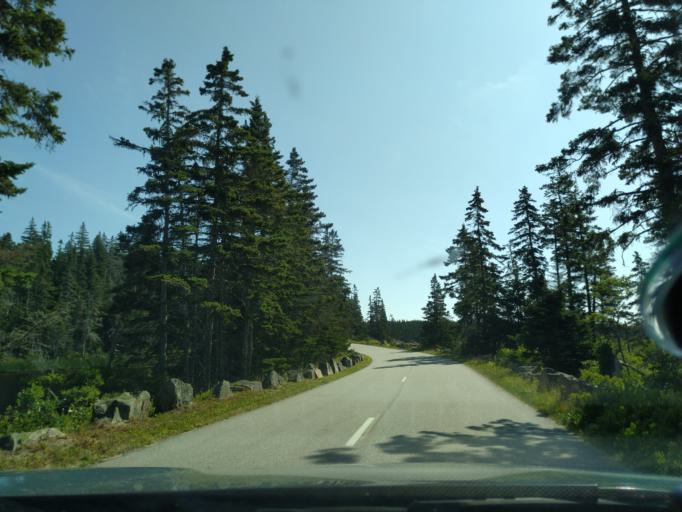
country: US
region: Maine
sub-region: Hancock County
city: Gouldsboro
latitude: 44.3623
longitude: -68.0410
